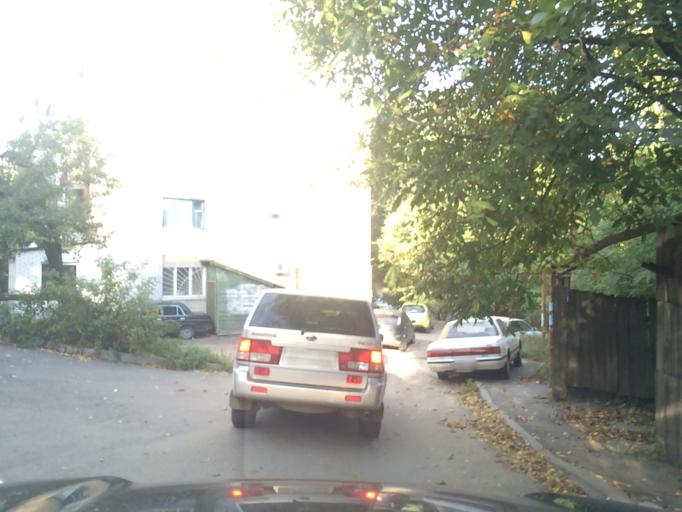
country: RU
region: Rostov
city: Rostov-na-Donu
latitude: 47.2114
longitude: 39.6899
